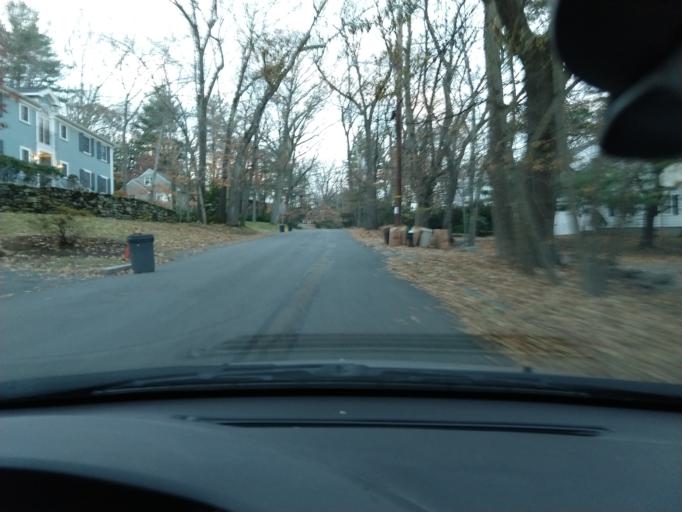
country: US
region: Massachusetts
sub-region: Middlesex County
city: Lexington
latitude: 42.4640
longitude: -71.2334
